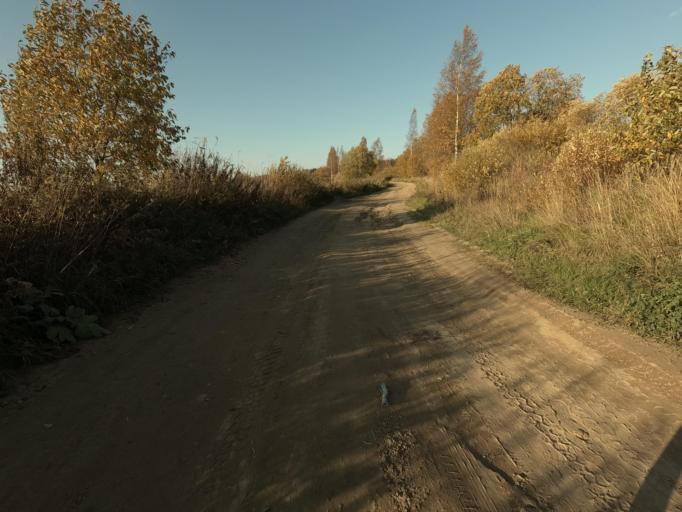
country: RU
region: Leningrad
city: Luppolovo
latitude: 60.1410
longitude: 30.2519
